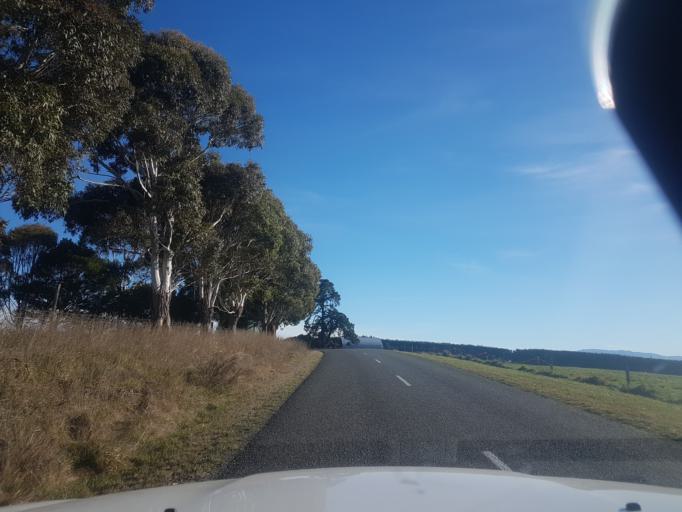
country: NZ
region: Canterbury
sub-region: Timaru District
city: Pleasant Point
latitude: -44.2476
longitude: 171.0753
